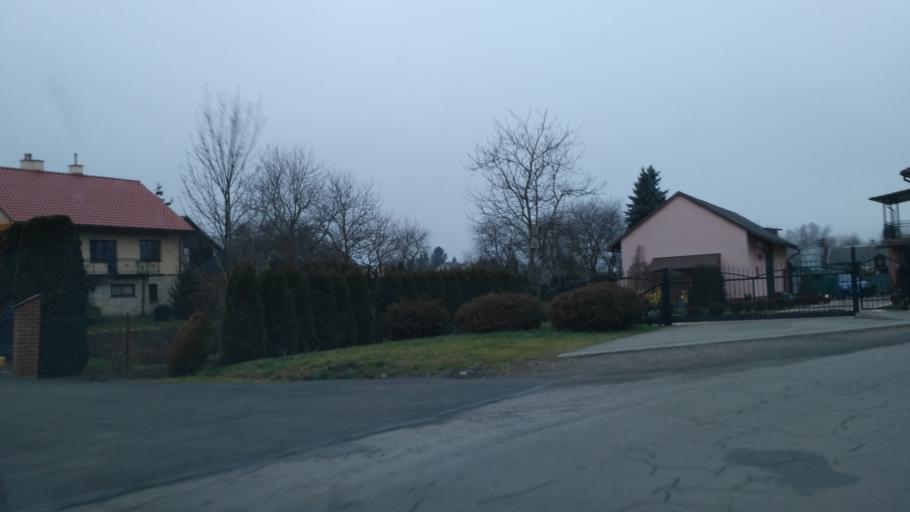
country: PL
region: Subcarpathian Voivodeship
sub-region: Powiat jaroslawski
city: Pawlosiow
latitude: 49.9662
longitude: 22.6479
